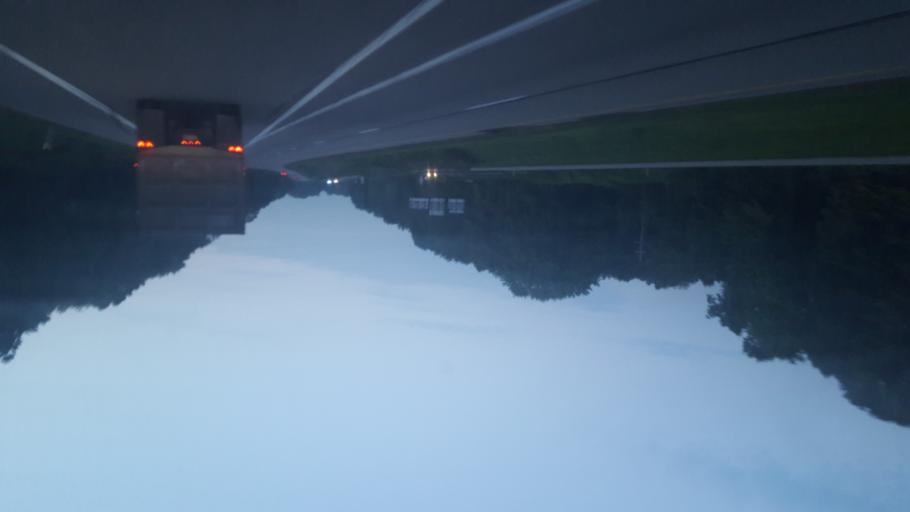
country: US
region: Pennsylvania
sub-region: Mercer County
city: Mercer
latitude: 41.2031
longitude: -80.1594
